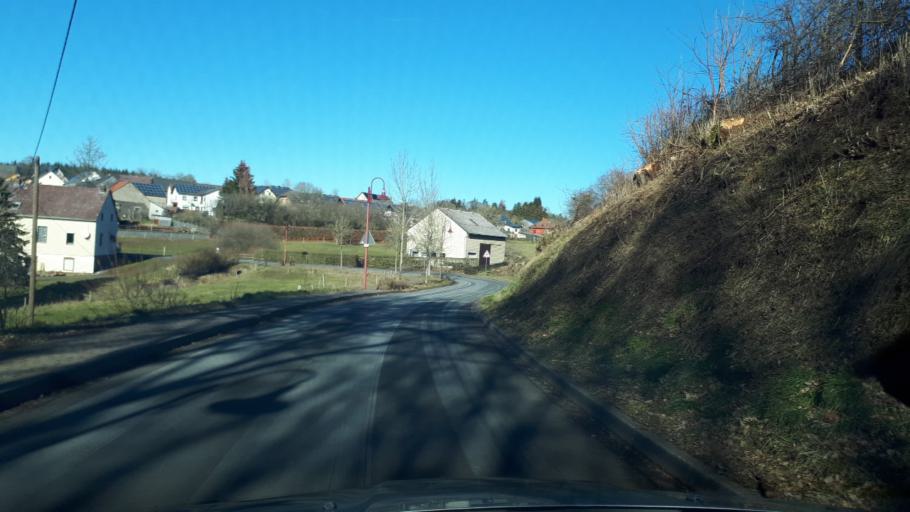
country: DE
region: Rheinland-Pfalz
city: Ellscheid
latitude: 50.1493
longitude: 6.9171
